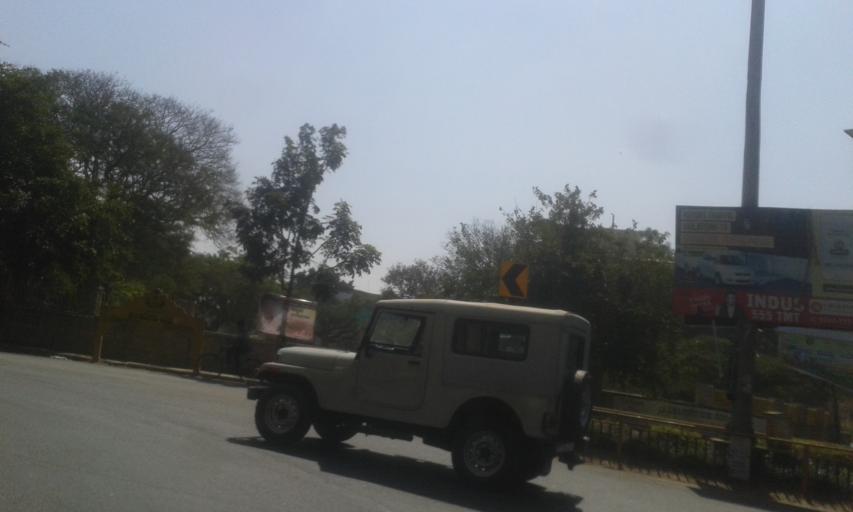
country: IN
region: Karnataka
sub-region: Bangalore Urban
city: Bangalore
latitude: 12.9407
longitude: 77.5770
